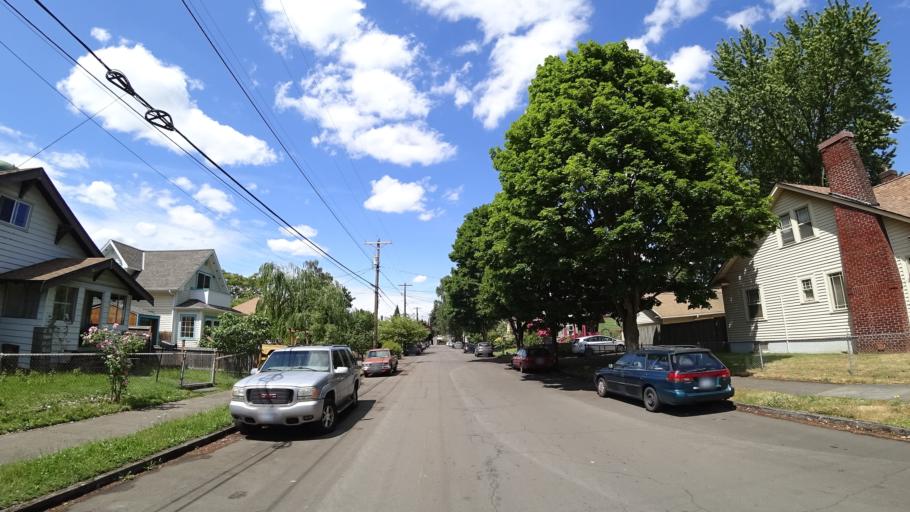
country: US
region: Oregon
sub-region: Multnomah County
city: Portland
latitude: 45.5612
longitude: -122.6801
